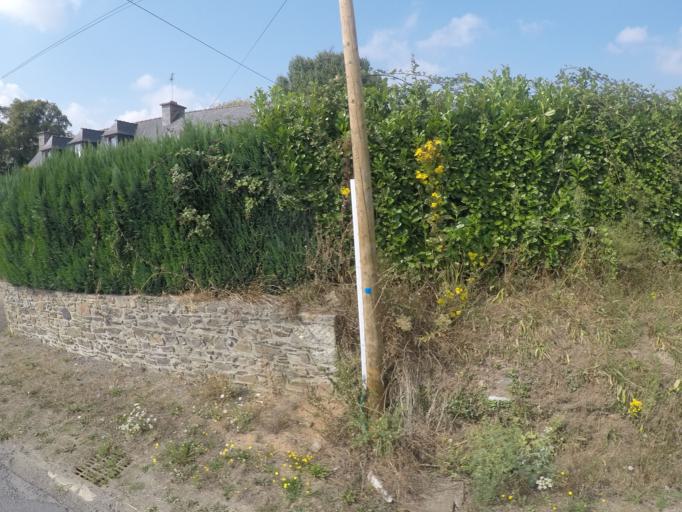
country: FR
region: Brittany
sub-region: Departement des Cotes-d'Armor
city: Tremuson
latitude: 48.5177
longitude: -2.8789
